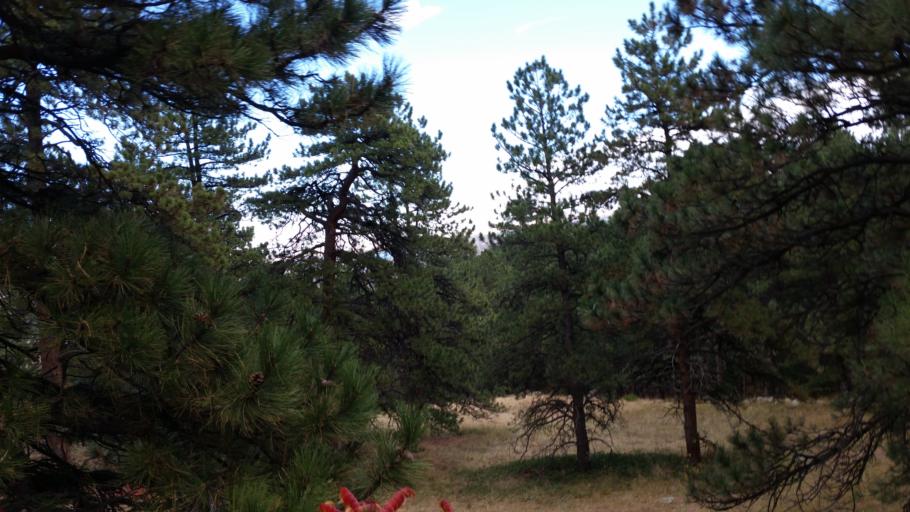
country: US
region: Colorado
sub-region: Boulder County
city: Boulder
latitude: 39.9938
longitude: -105.2894
